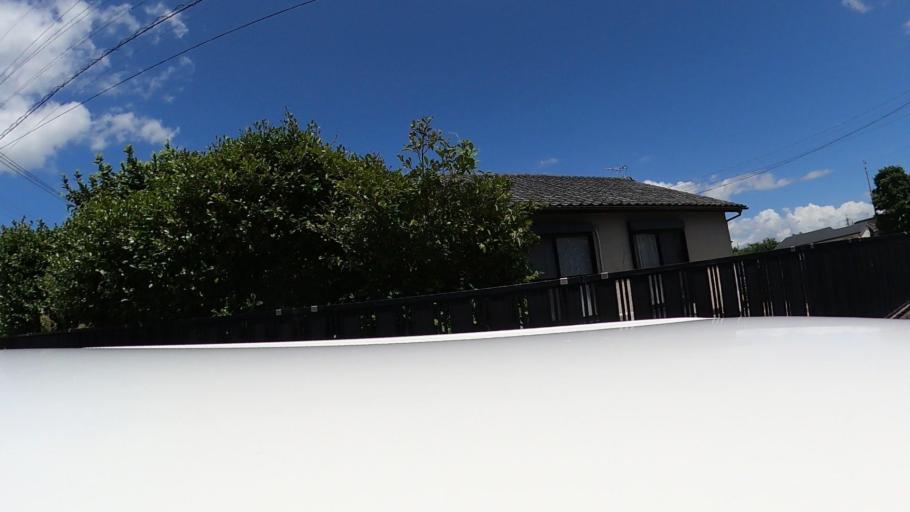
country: JP
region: Miyazaki
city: Miyazaki-shi
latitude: 31.9899
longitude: 131.4528
